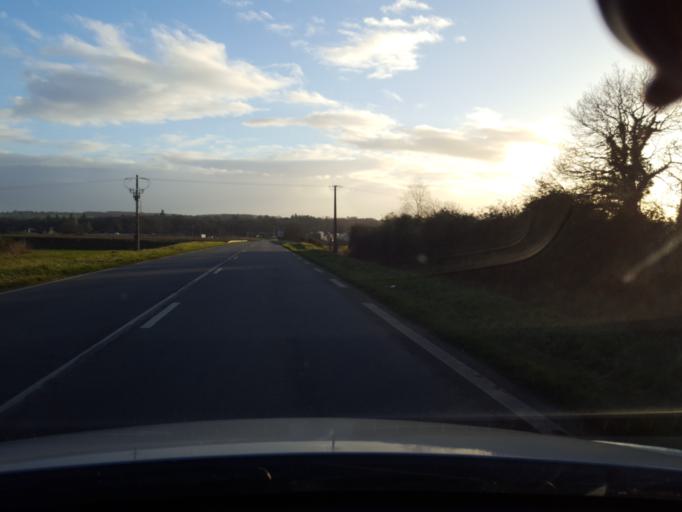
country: FR
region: Brittany
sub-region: Departement d'Ille-et-Vilaine
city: Guignen
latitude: 47.9264
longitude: -1.8526
